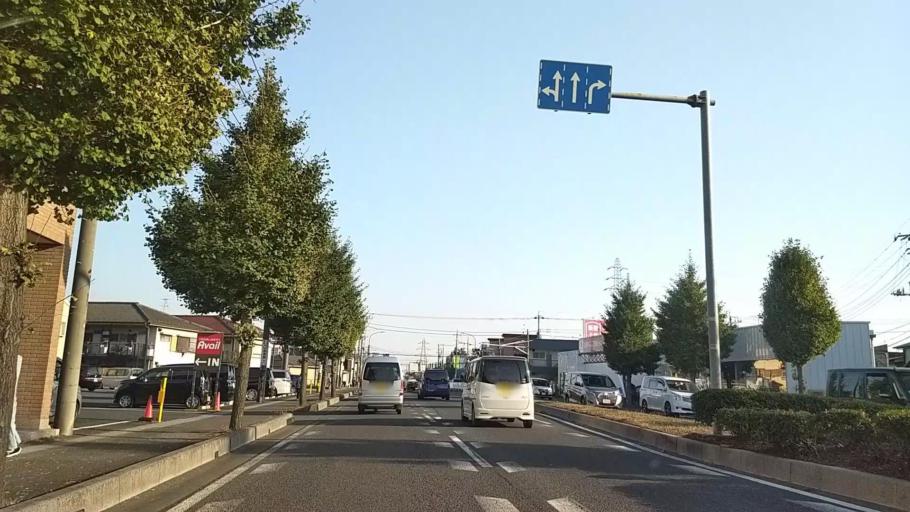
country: JP
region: Saitama
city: Sayama
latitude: 35.8068
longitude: 139.4075
